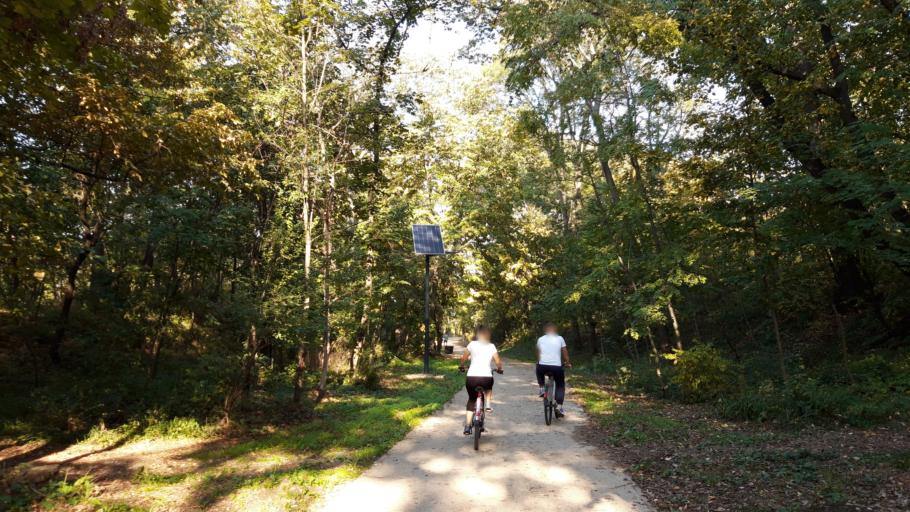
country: RS
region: Autonomna Pokrajina Vojvodina
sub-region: Juznobacki Okrug
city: Novi Sad
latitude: 45.2302
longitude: 19.8498
